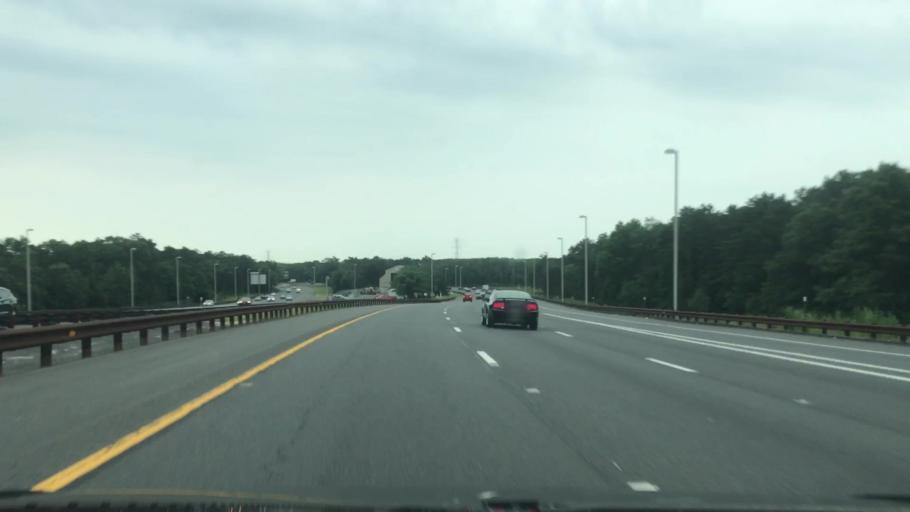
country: US
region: New Jersey
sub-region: Ocean County
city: Silver Ridge
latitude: 39.9869
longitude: -74.2114
